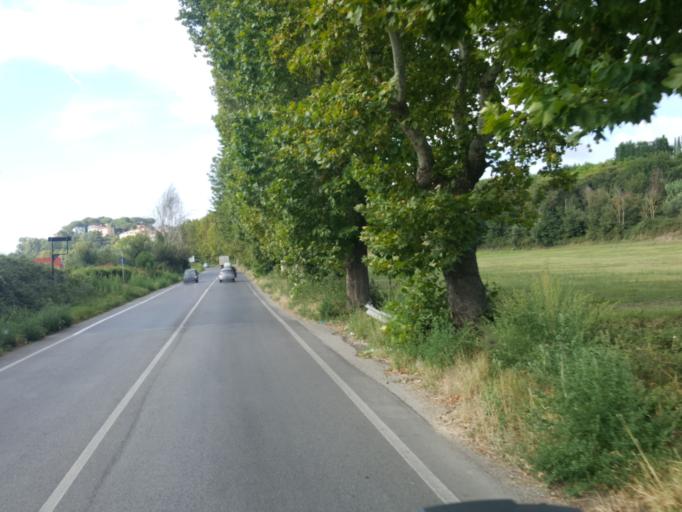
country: IT
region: Latium
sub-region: Citta metropolitana di Roma Capitale
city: Girardi-Bellavista-Terrazze
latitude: 42.1112
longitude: 12.5855
